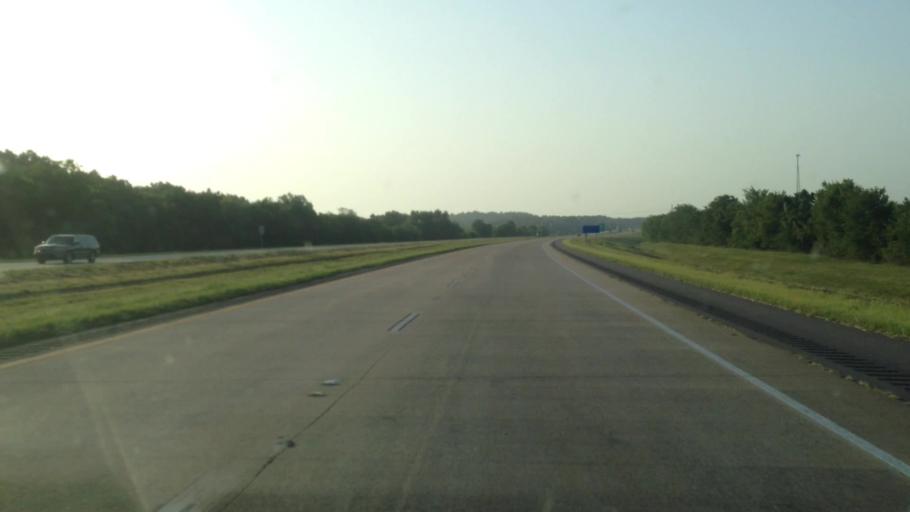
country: US
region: Louisiana
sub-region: Grant Parish
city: Colfax
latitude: 31.5011
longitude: -92.8720
